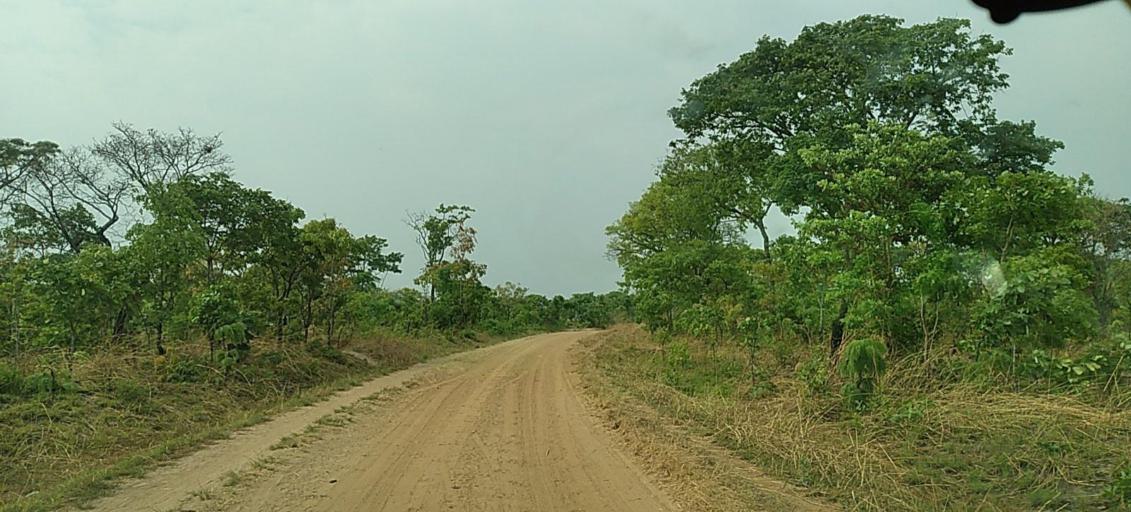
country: ZM
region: North-Western
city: Kabompo
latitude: -13.4676
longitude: 24.4307
